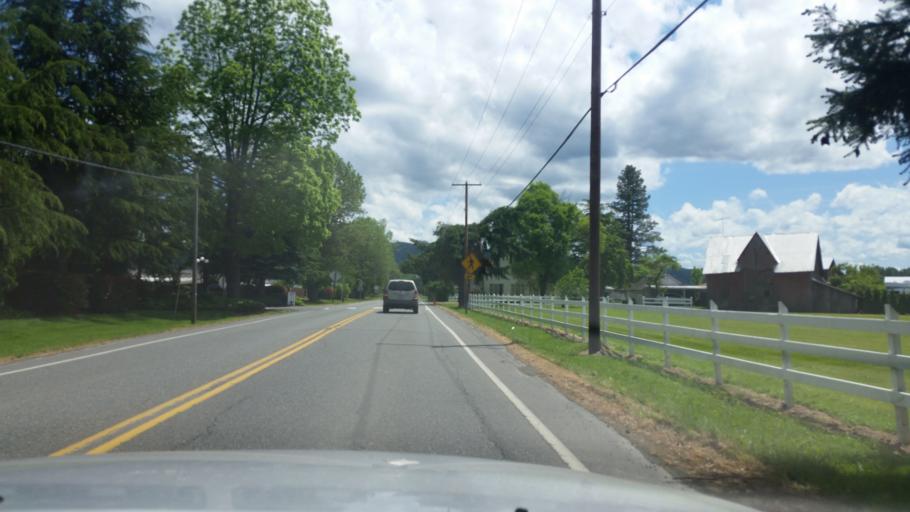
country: US
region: Washington
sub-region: Pierce County
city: Orting
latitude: 47.0902
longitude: -122.1982
